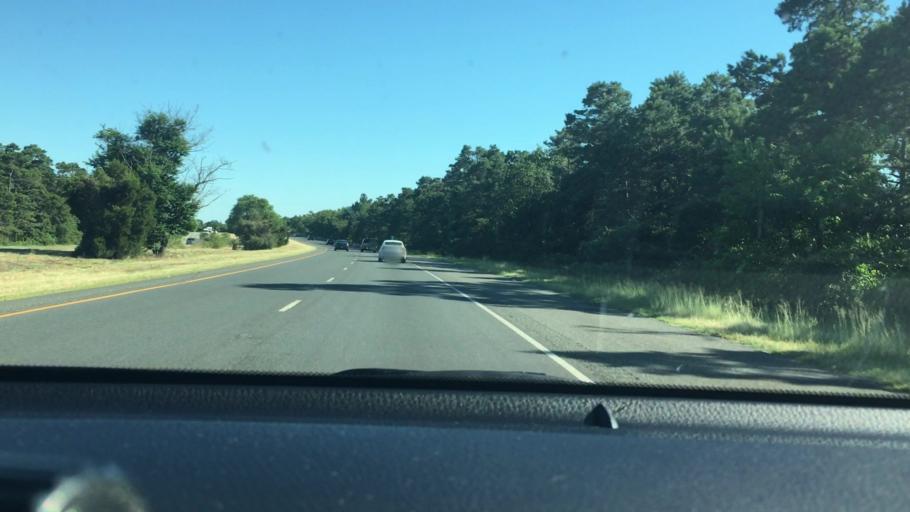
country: US
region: New Jersey
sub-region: Cumberland County
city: South Vineland
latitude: 39.4685
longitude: -75.0745
